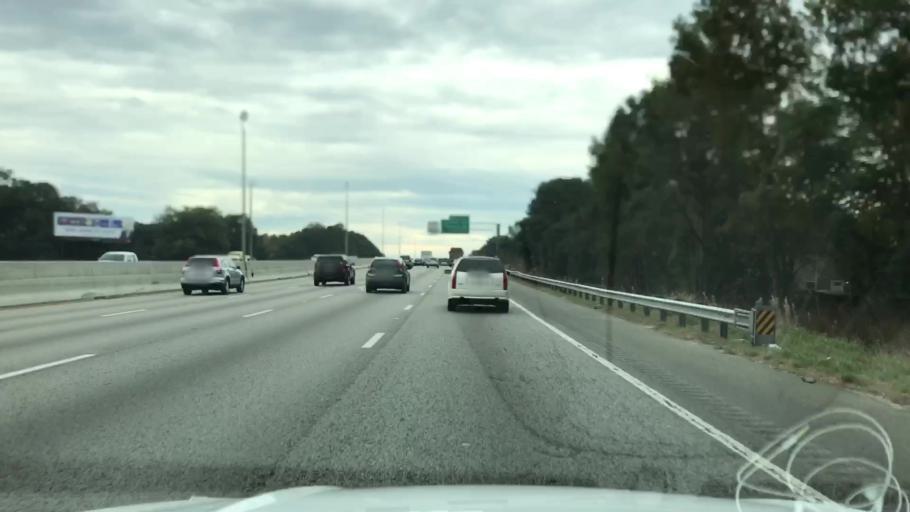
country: US
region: South Carolina
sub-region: Berkeley County
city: Hanahan
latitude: 32.9225
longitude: -80.0391
